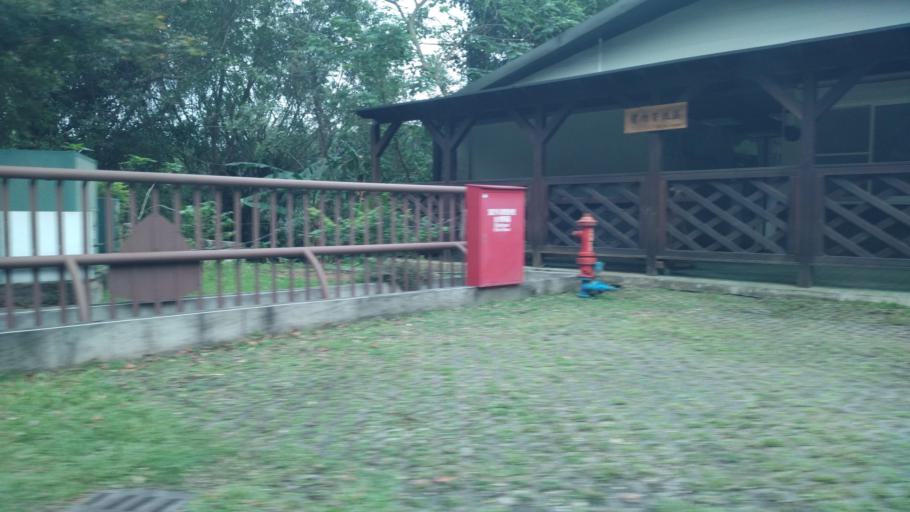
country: TW
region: Taiwan
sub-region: Hualien
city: Hualian
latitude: 23.9192
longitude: 121.5015
